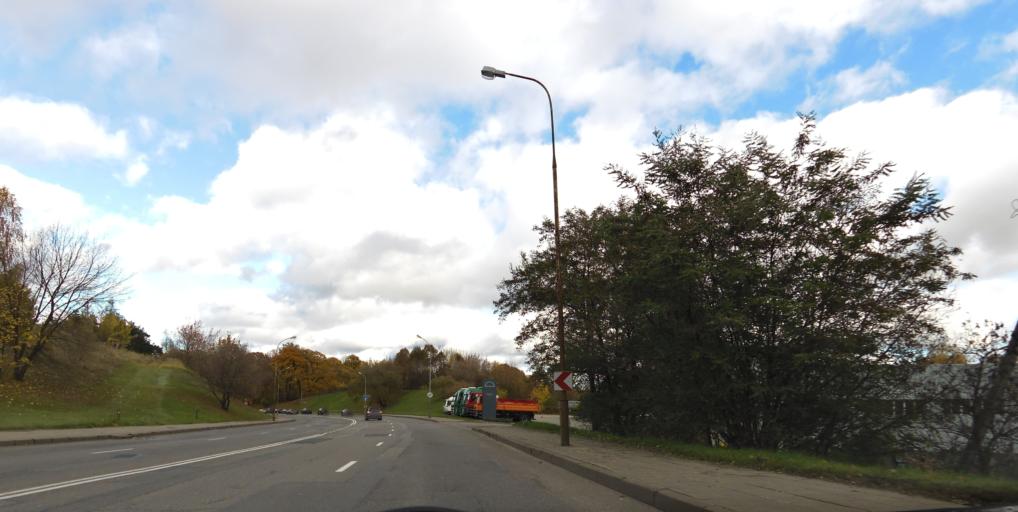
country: LT
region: Vilnius County
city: Rasos
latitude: 54.6646
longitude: 25.3046
